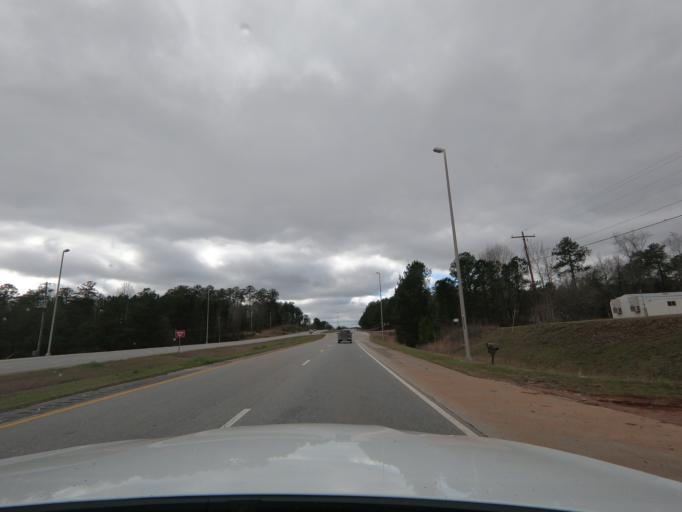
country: US
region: Alabama
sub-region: Russell County
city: Ladonia
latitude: 32.4092
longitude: -85.0496
